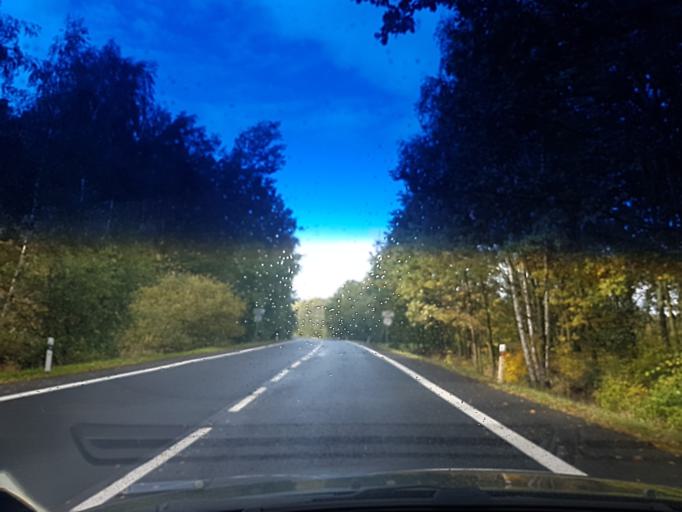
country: CZ
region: Karlovarsky
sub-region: Okres Cheb
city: Cheb
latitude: 50.0751
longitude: 12.3482
